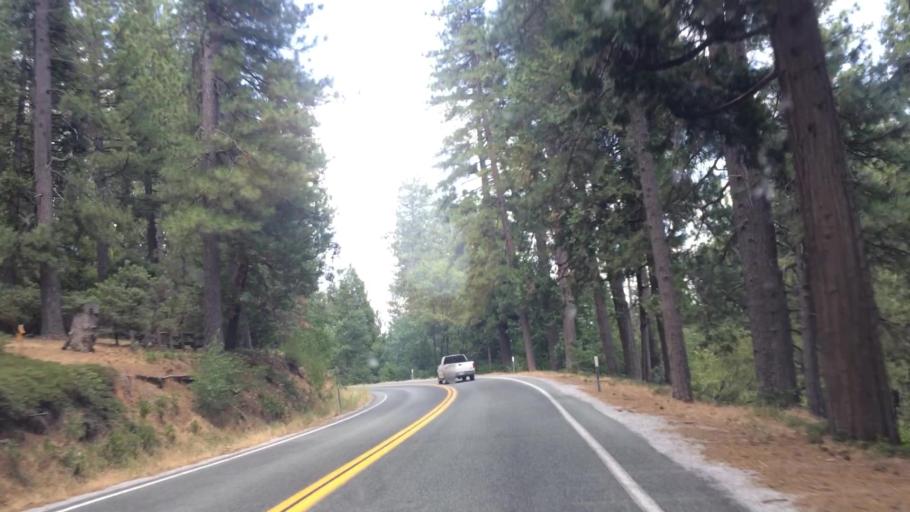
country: US
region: California
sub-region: Amador County
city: Pioneer
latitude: 38.4994
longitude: -120.5033
